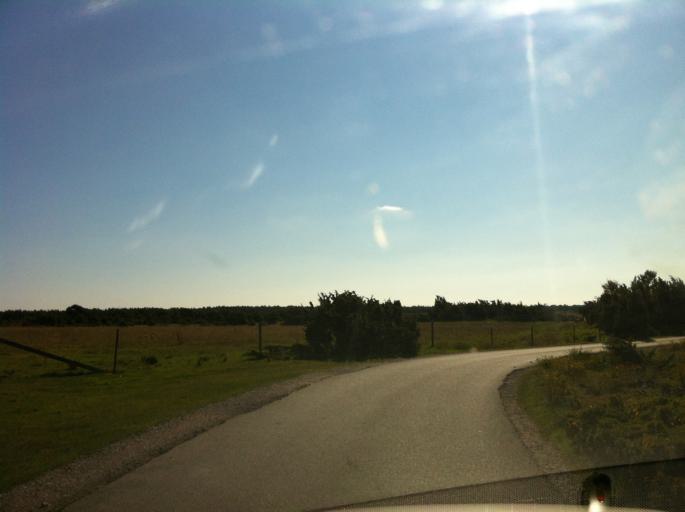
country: SE
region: Gotland
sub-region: Gotland
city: Slite
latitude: 57.9879
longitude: 19.1674
